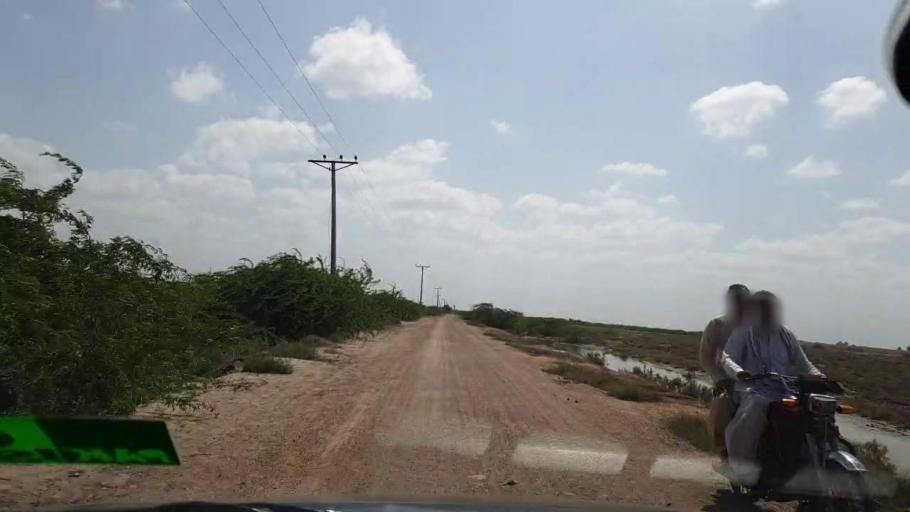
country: PK
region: Sindh
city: Kadhan
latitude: 24.6025
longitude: 69.1852
